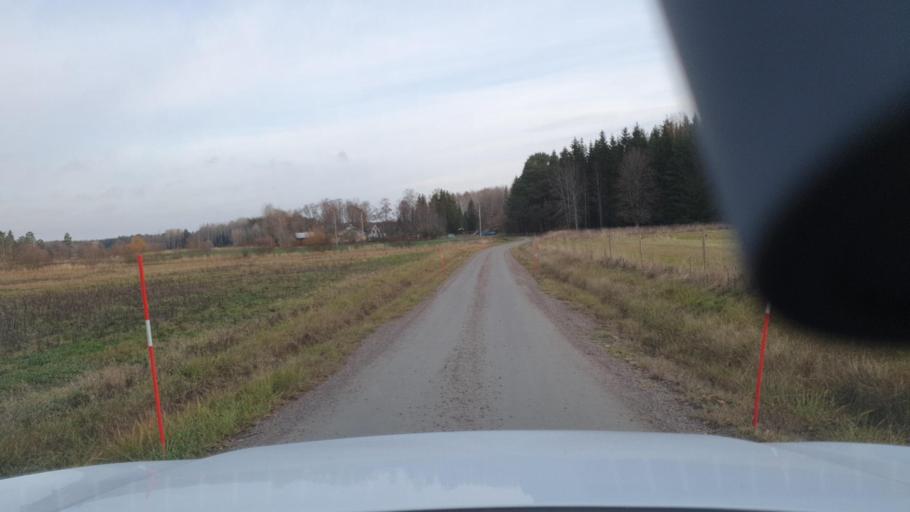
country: SE
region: Uppsala
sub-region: Tierps Kommun
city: Karlholmsbruk
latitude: 60.4844
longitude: 17.5221
